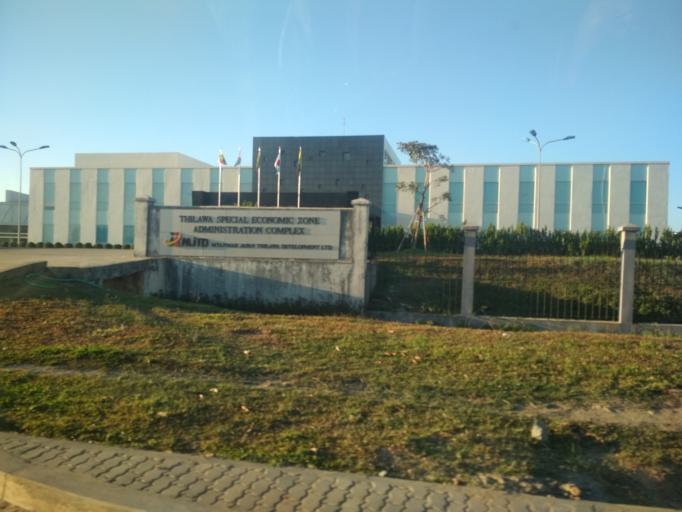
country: MM
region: Yangon
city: Syriam
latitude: 16.6693
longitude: 96.2751
